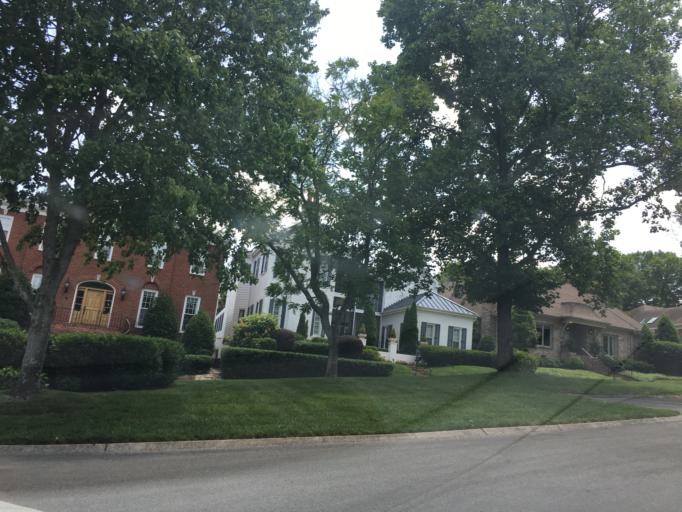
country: US
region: Tennessee
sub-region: Davidson County
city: Belle Meade
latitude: 36.1043
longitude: -86.8273
